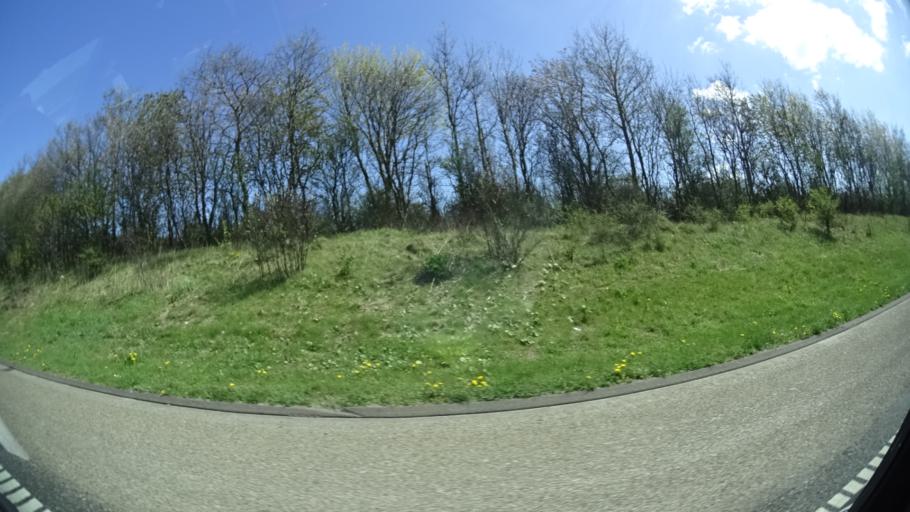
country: DK
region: Central Jutland
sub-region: Arhus Kommune
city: Framlev
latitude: 56.1382
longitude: 10.0376
